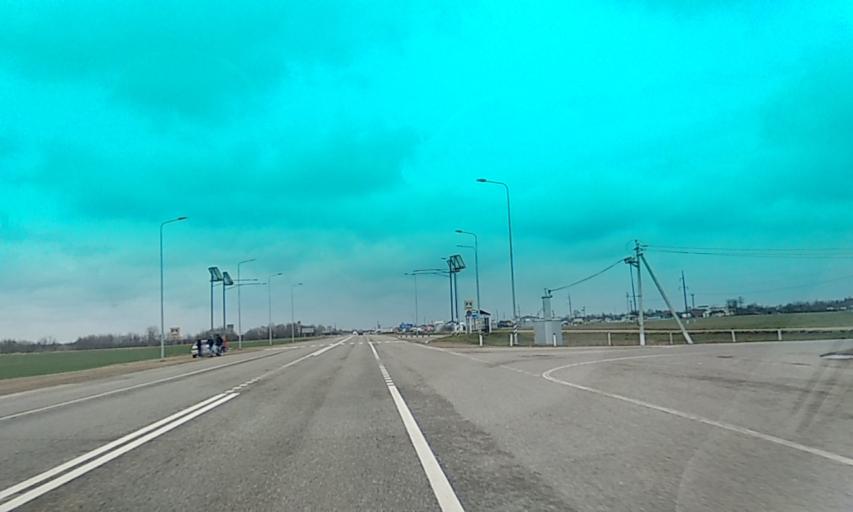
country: RU
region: Krasnodarskiy
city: Velikovechnoye
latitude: 44.9367
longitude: 39.7701
